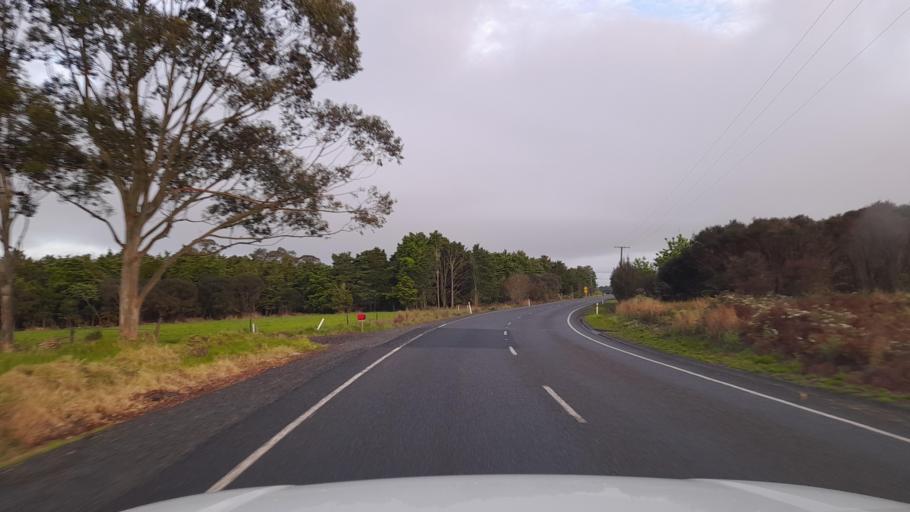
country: NZ
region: Northland
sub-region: Kaipara District
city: Dargaville
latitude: -35.7110
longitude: 173.9418
